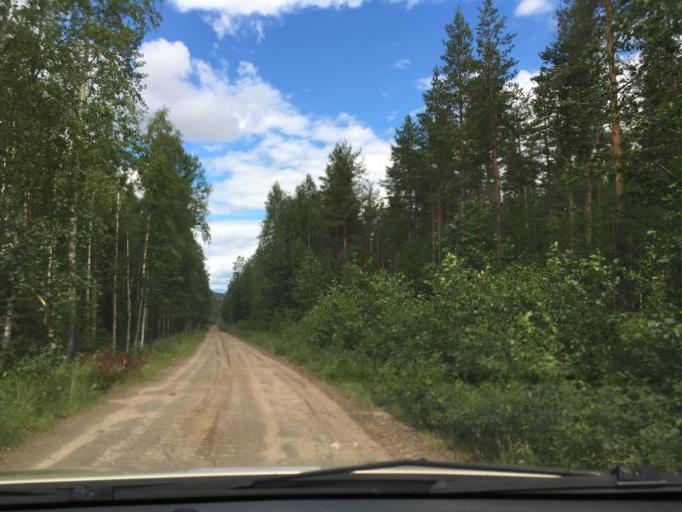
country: SE
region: Norrbotten
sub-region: Overkalix Kommun
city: OEverkalix
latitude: 66.1354
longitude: 22.7842
